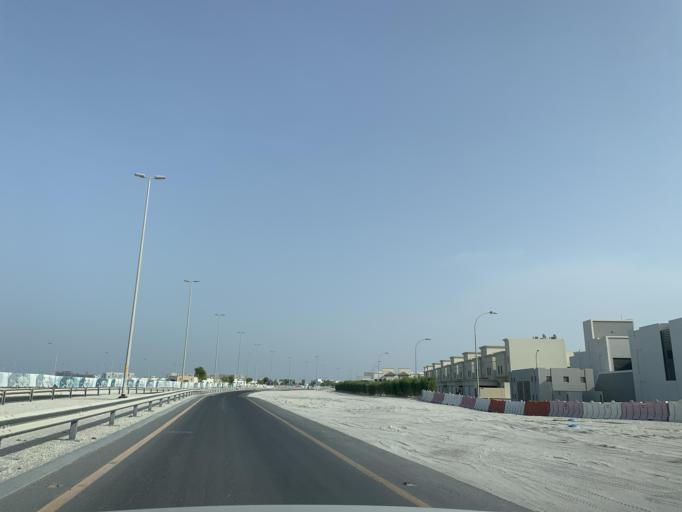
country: BH
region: Muharraq
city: Al Muharraq
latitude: 26.3200
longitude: 50.6299
